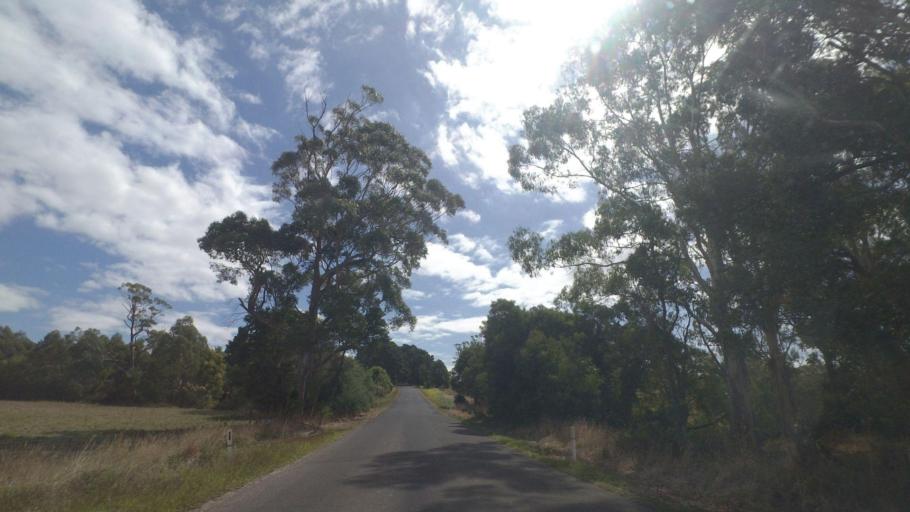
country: AU
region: Victoria
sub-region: Cardinia
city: Bunyip
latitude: -38.3081
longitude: 145.7652
